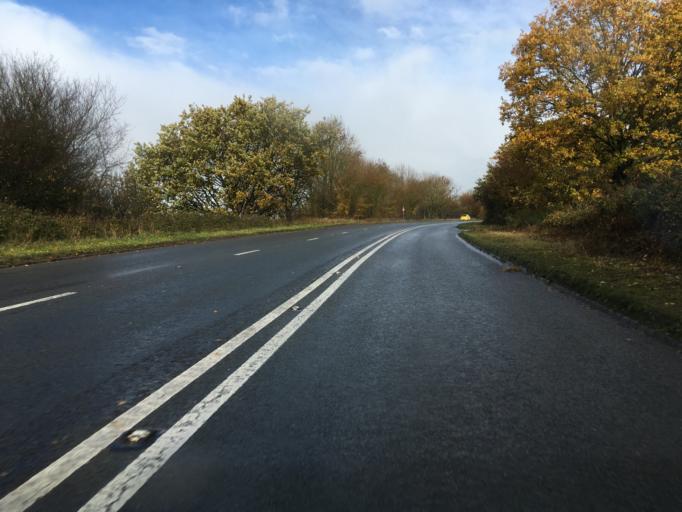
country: GB
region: England
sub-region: South Gloucestershire
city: Cold Ashton
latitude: 51.4513
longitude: -2.3997
